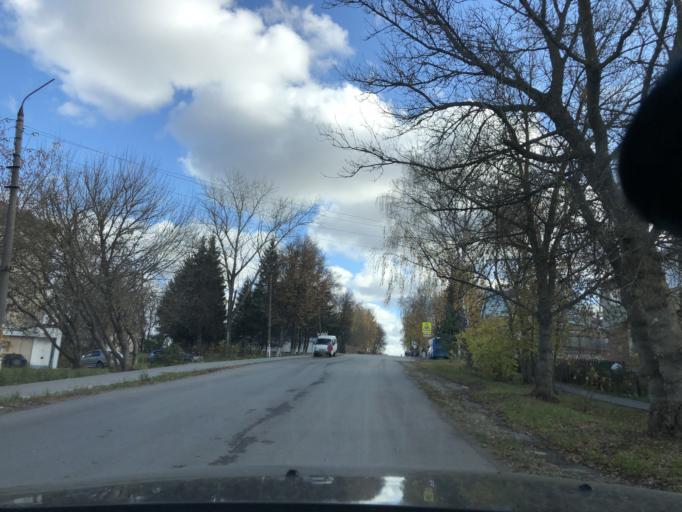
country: RU
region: Tula
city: Gorelki
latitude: 54.2959
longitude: 37.5691
